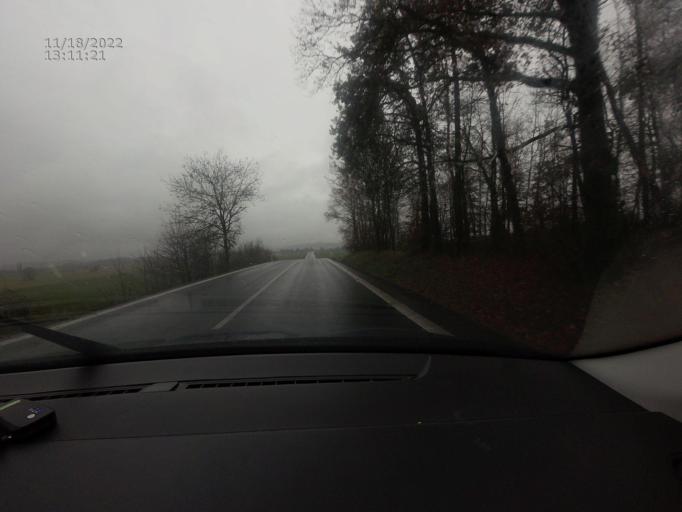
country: CZ
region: Plzensky
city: Hradek
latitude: 49.3278
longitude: 13.5832
